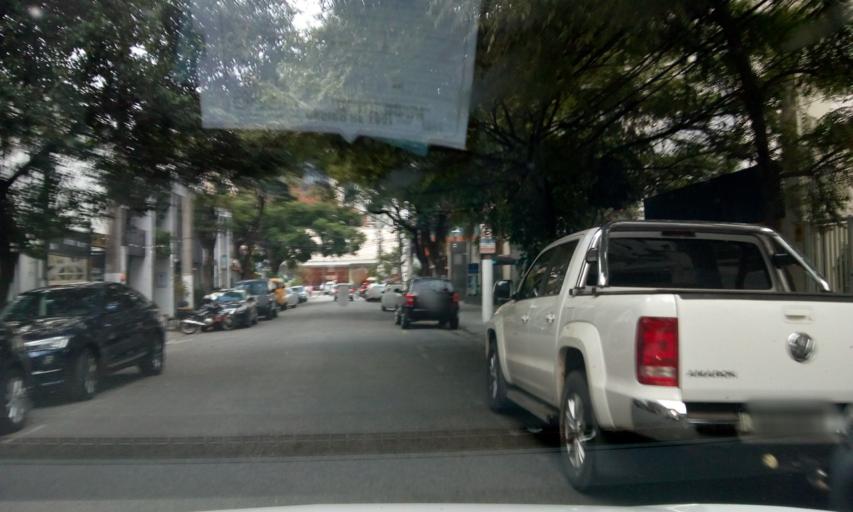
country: BR
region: Sao Paulo
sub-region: Sao Paulo
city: Sao Paulo
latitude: -23.5868
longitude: -46.6784
